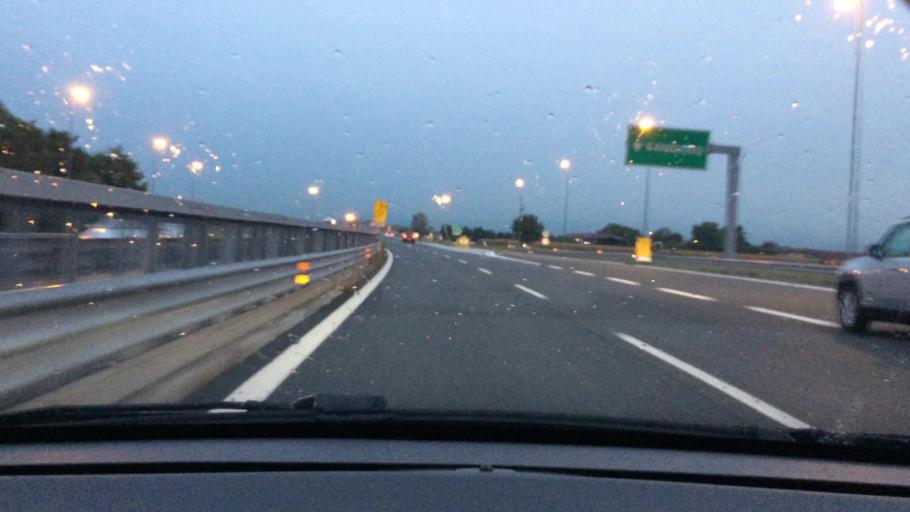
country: IT
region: Piedmont
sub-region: Provincia di Torino
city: Pasta
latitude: 44.9854
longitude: 7.5556
